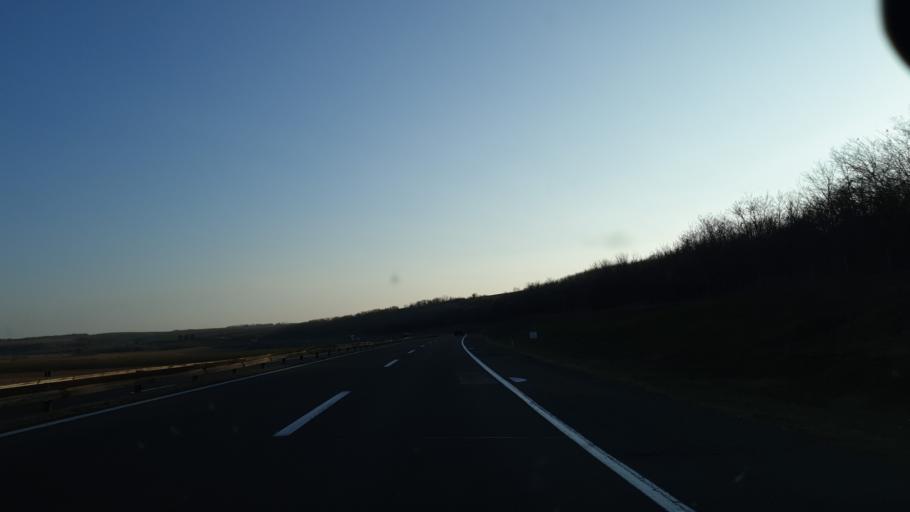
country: RS
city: Lugavcina
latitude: 44.4985
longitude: 21.0231
